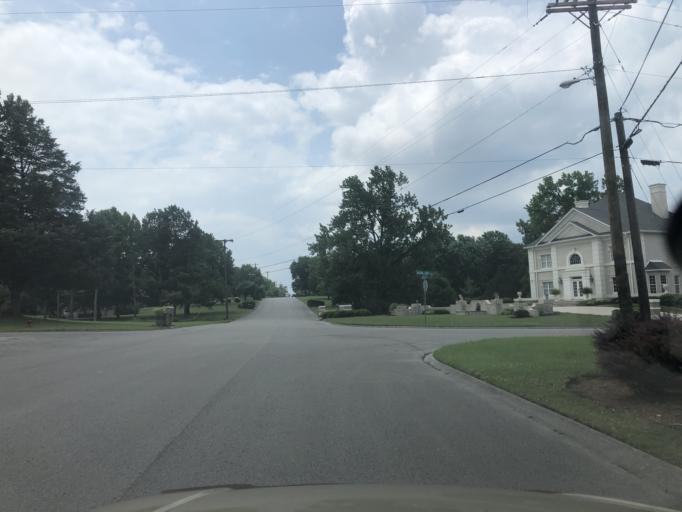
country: US
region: Tennessee
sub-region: Davidson County
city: Lakewood
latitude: 36.2389
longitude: -86.6100
